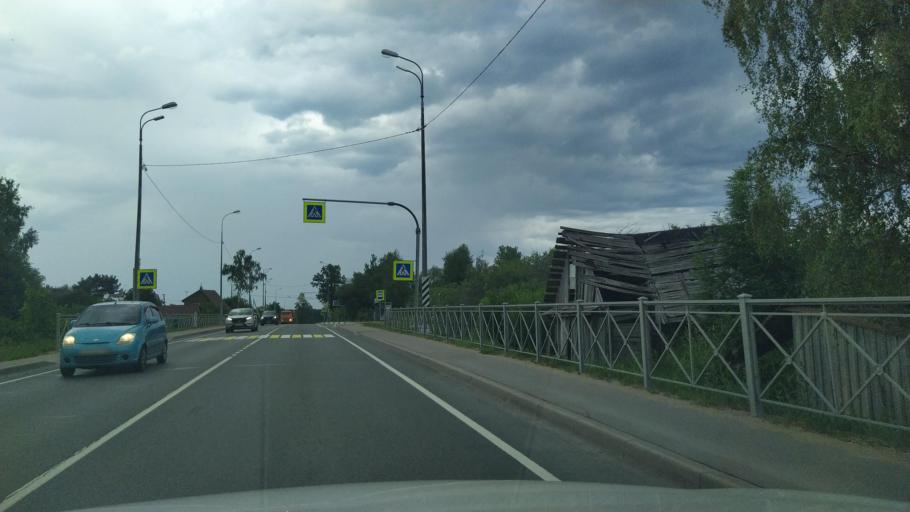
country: RU
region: St.-Petersburg
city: Bol'shaya Izhora
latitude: 59.9342
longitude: 29.5714
